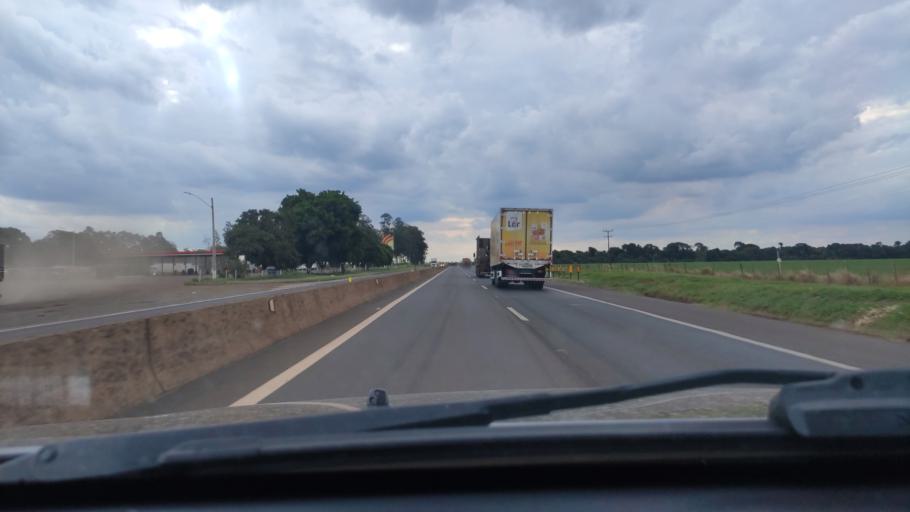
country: BR
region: Sao Paulo
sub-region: Palmital
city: Palmital
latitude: -22.8367
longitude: -50.0202
